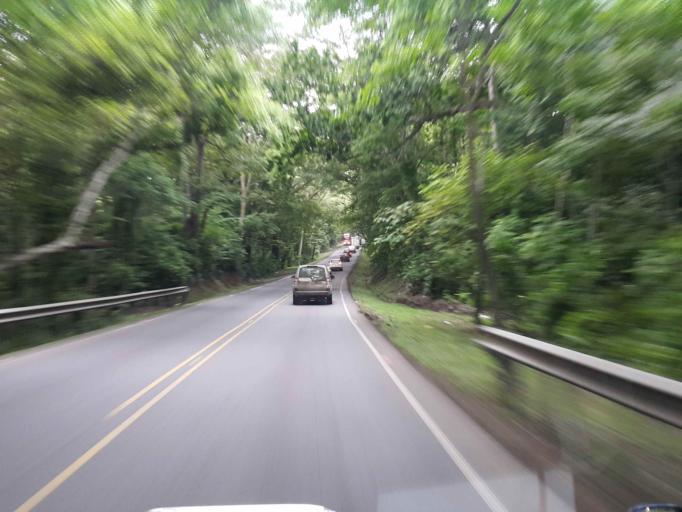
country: CR
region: Puntarenas
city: Miramar
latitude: 10.0434
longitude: -84.7496
